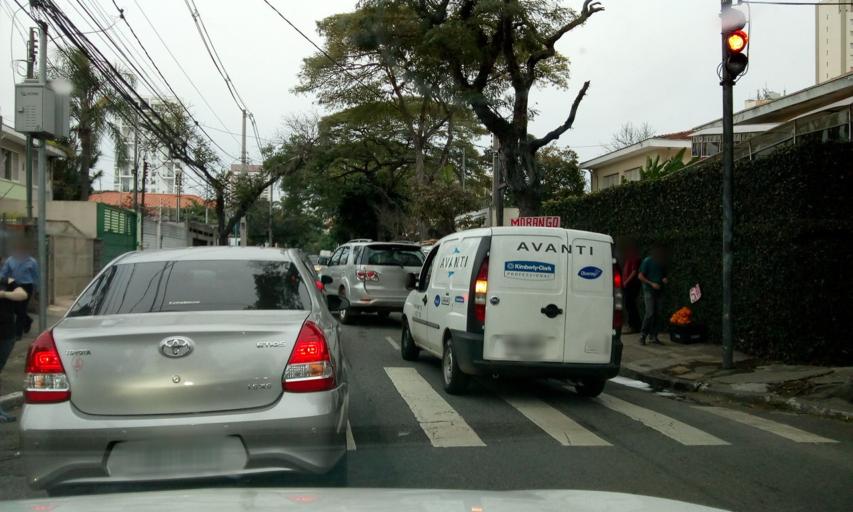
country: BR
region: Sao Paulo
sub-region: Sao Paulo
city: Sao Paulo
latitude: -23.6080
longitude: -46.6862
